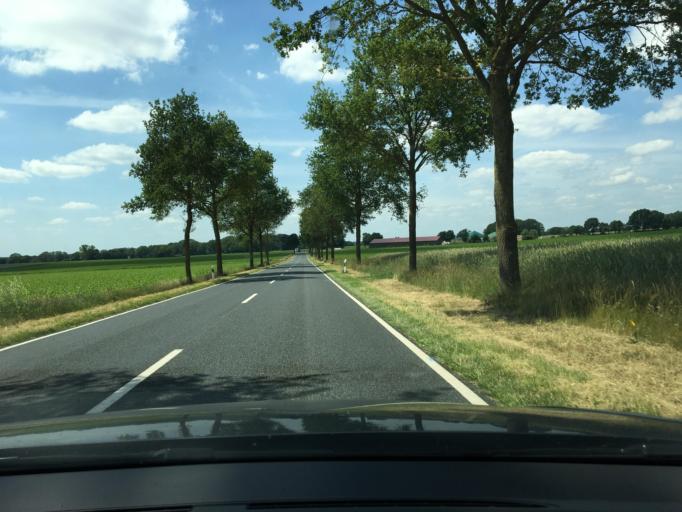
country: DE
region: Lower Saxony
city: Zeven
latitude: 53.2617
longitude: 9.2703
